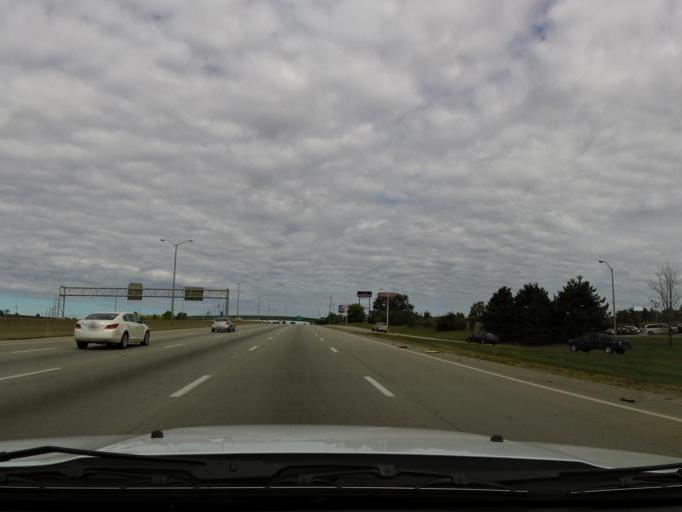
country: US
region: Kentucky
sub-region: Boone County
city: Florence
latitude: 38.9871
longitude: -84.6423
